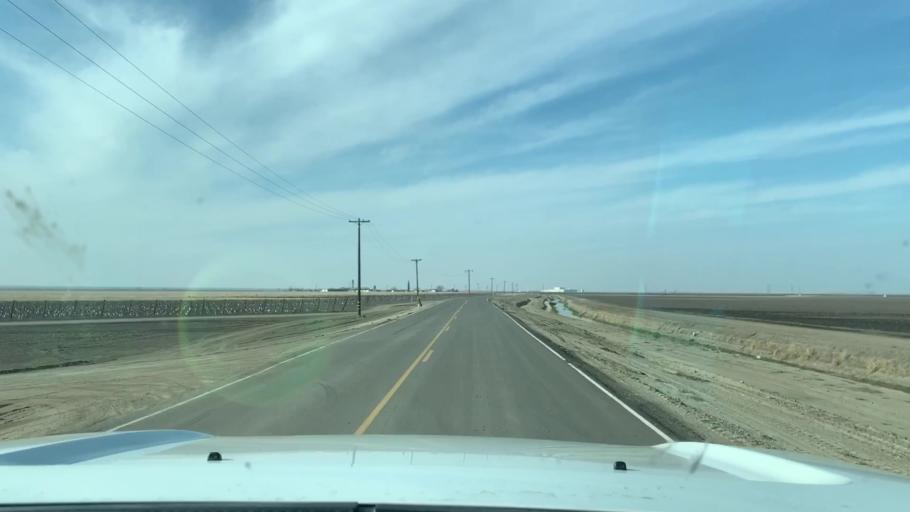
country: US
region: California
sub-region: Kern County
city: Buttonwillow
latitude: 35.4781
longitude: -119.5886
